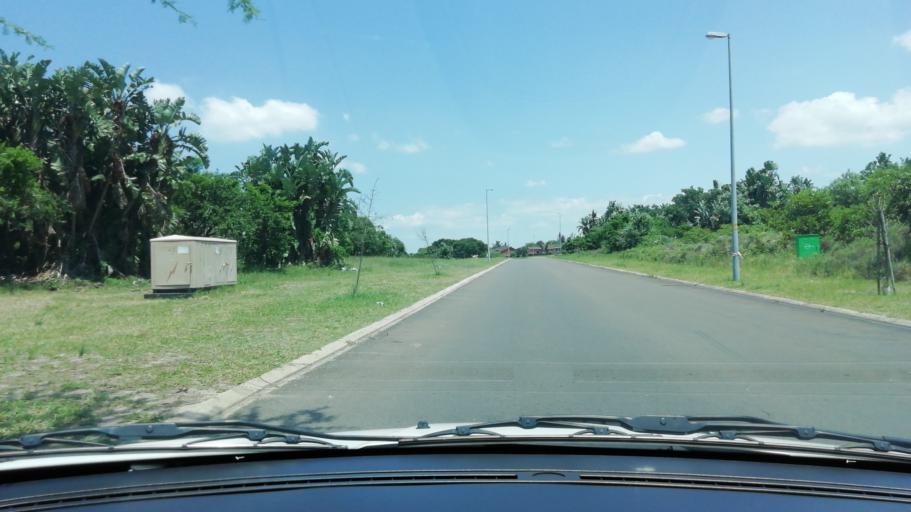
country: ZA
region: KwaZulu-Natal
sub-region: uThungulu District Municipality
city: Richards Bay
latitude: -28.7336
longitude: 32.0499
